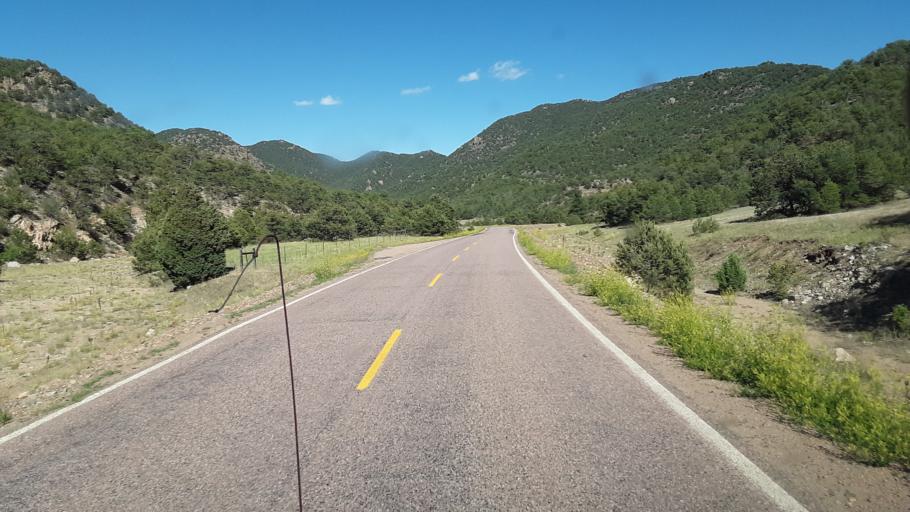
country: US
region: Colorado
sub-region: Fremont County
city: Canon City
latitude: 38.4125
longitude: -105.4301
